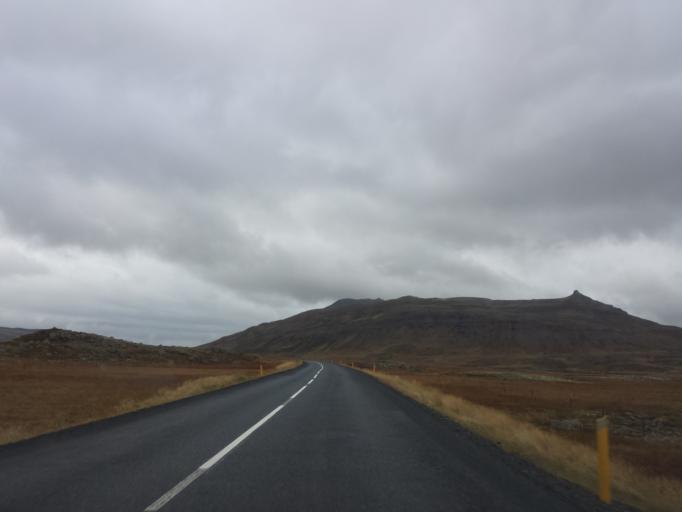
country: IS
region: West
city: Stykkisholmur
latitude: 64.8697
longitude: -22.7621
